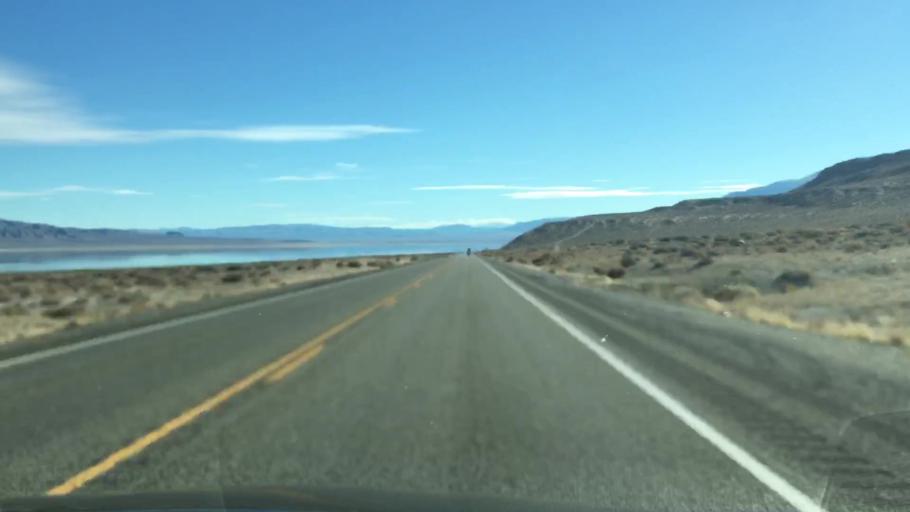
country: US
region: Nevada
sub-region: Mineral County
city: Hawthorne
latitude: 38.7927
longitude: -118.7561
